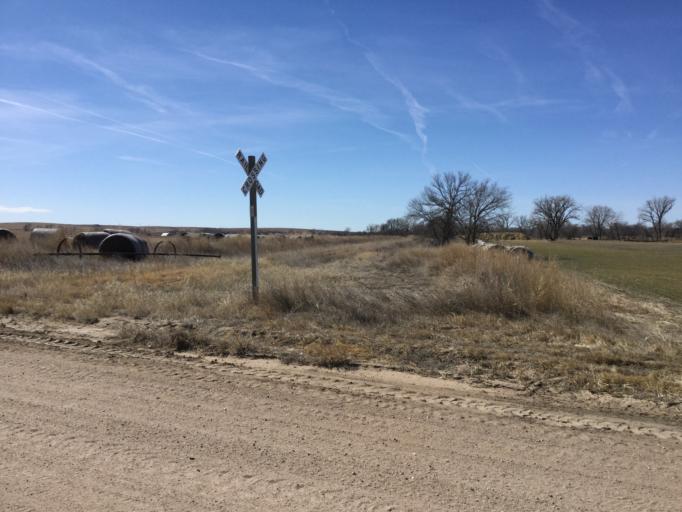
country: US
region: Kansas
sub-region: Rawlins County
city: Atwood
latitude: 39.9042
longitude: -100.7962
